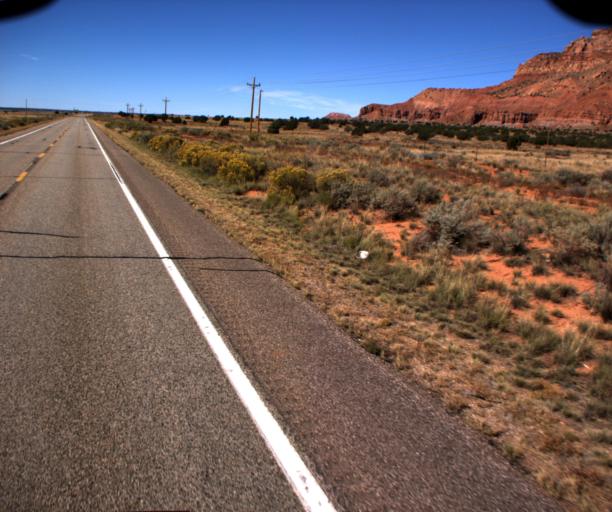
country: US
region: Arizona
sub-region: Mohave County
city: Colorado City
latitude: 36.8583
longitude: -112.7975
